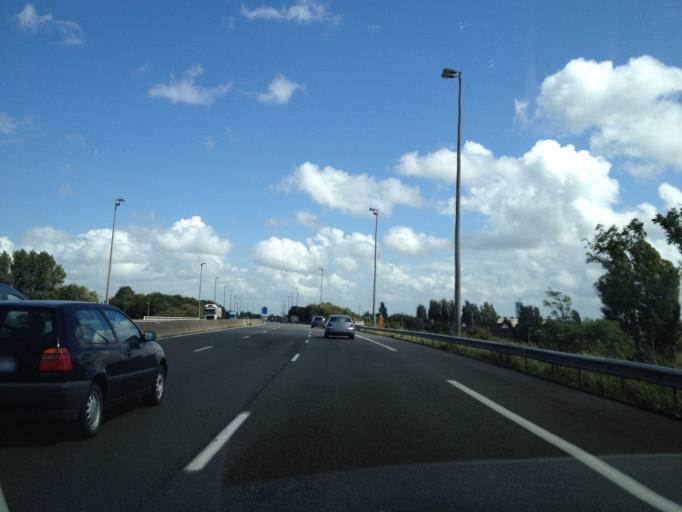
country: FR
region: Nord-Pas-de-Calais
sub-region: Departement du Pas-de-Calais
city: Calais
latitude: 50.9366
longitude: 1.8480
